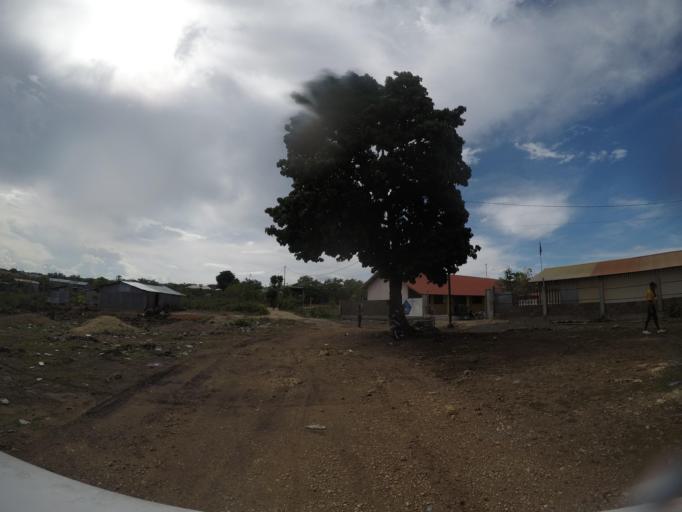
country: TL
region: Baucau
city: Baucau
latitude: -8.4809
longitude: 126.4554
